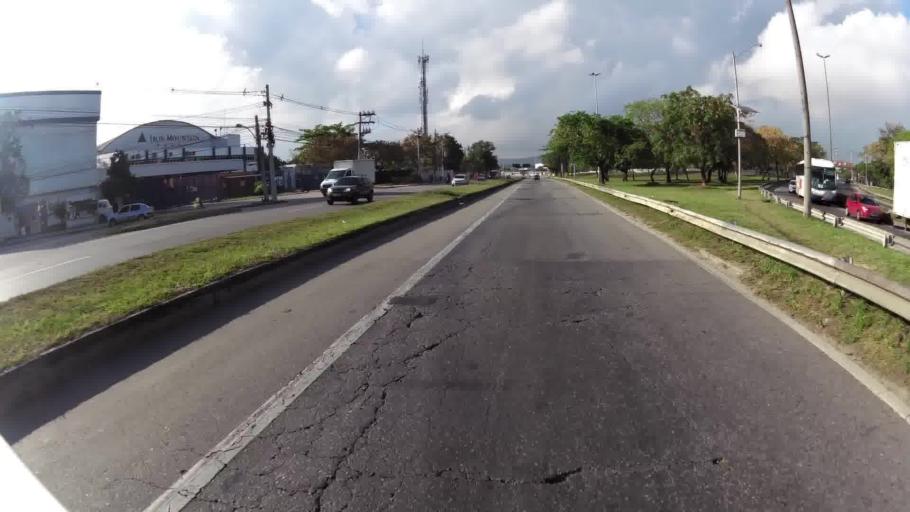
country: BR
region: Rio de Janeiro
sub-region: Duque De Caxias
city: Duque de Caxias
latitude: -22.8137
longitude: -43.2876
